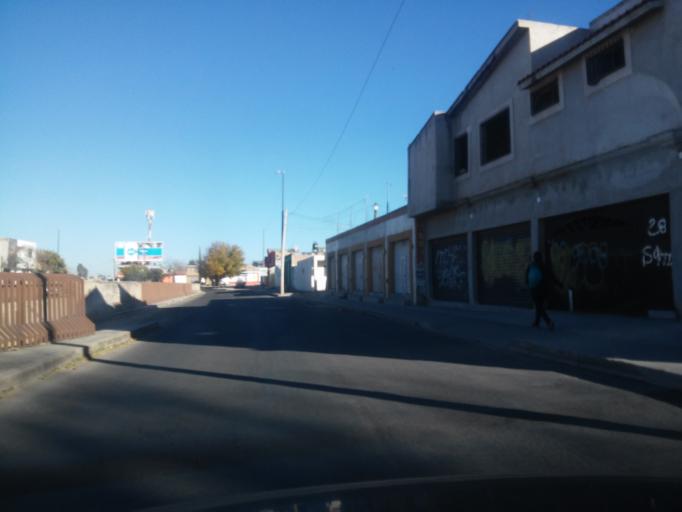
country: MX
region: Durango
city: Victoria de Durango
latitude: 24.0155
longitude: -104.6396
